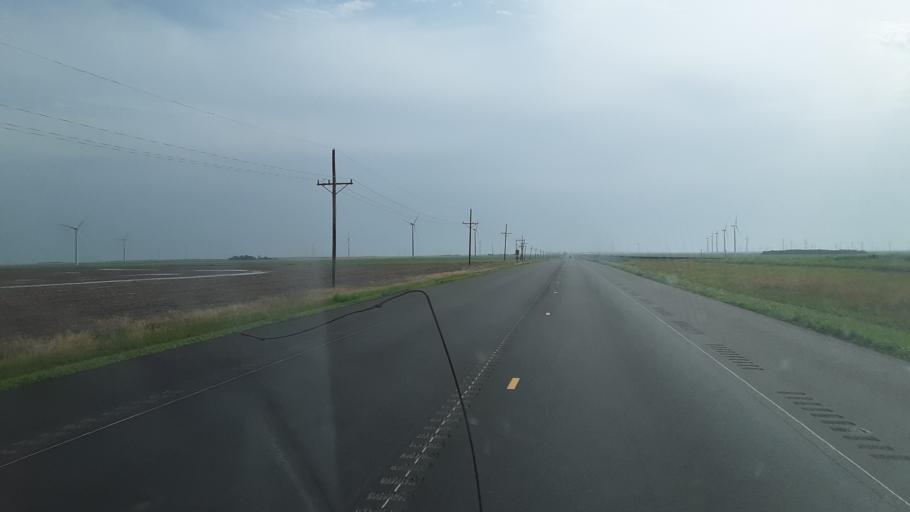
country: US
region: Kansas
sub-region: Ford County
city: Dodge City
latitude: 37.8020
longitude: -99.8547
